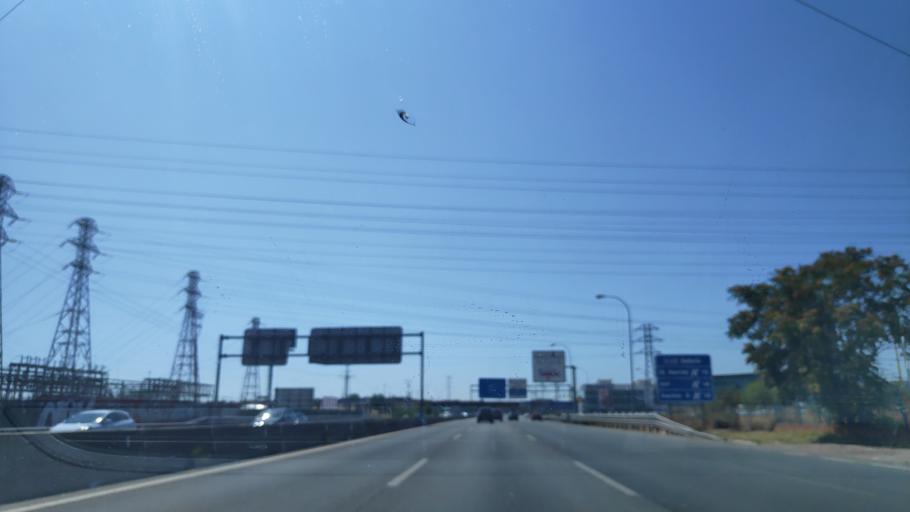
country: ES
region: Madrid
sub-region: Provincia de Madrid
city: Villaverde
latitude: 40.3355
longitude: -3.7247
